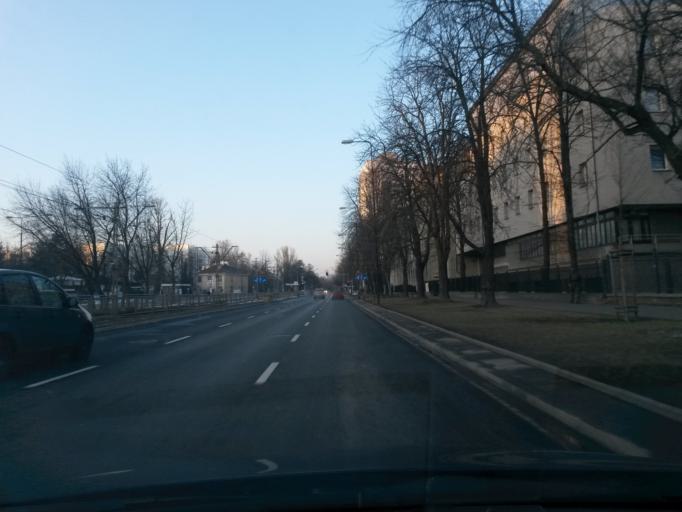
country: PL
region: Masovian Voivodeship
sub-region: Warszawa
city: Ochota
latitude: 52.2046
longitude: 20.9998
